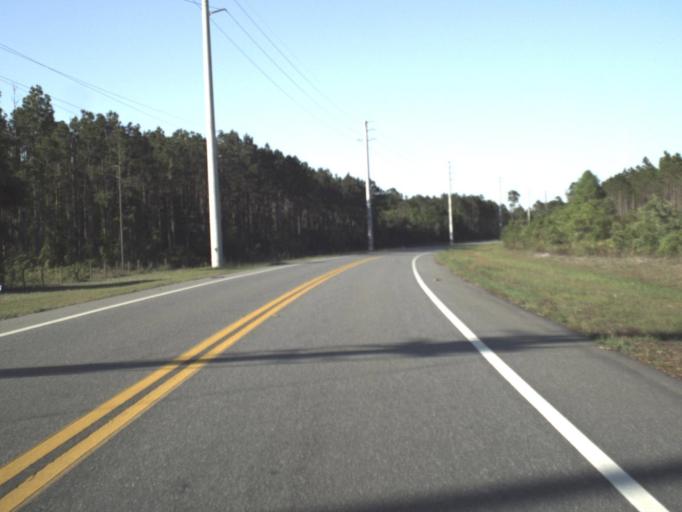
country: US
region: Florida
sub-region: Gadsden County
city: Gretna
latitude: 30.4419
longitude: -84.7693
